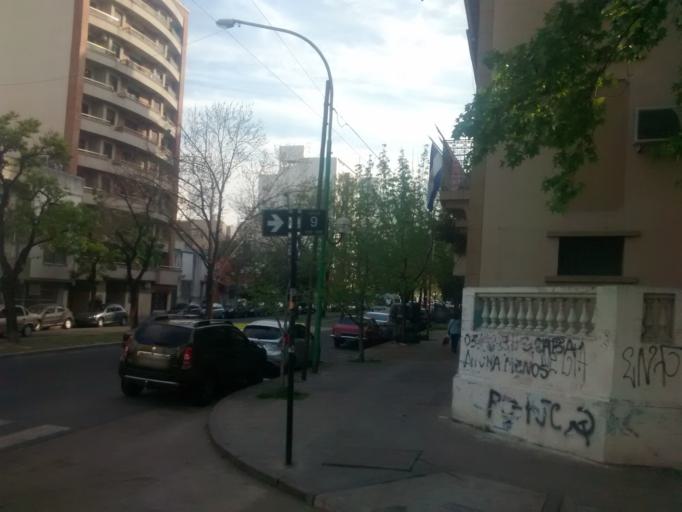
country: AR
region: Buenos Aires
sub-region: Partido de La Plata
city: La Plata
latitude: -34.9227
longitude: -57.9436
